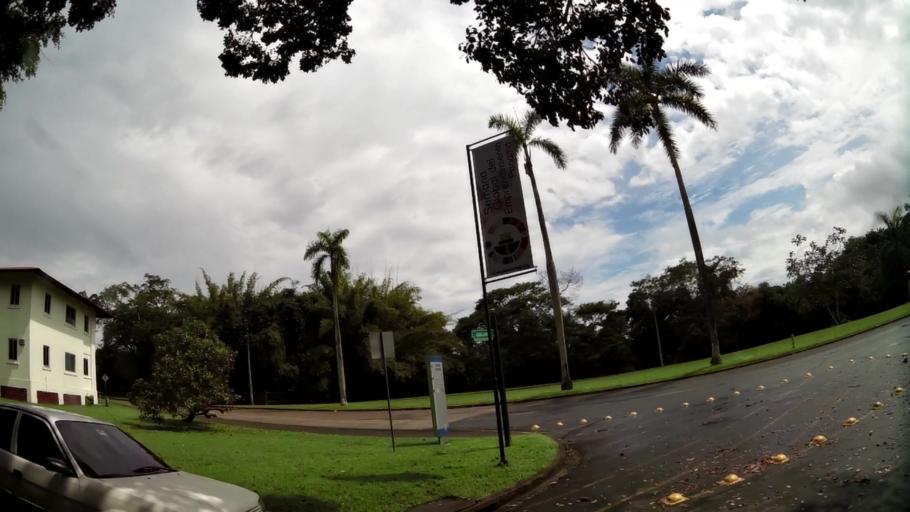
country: PA
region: Panama
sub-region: Distrito de Panama
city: Ancon
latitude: 8.9966
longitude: -79.5795
